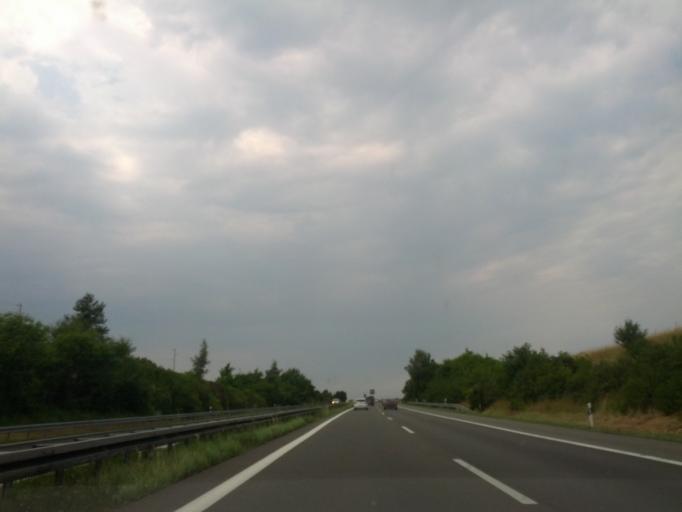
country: DE
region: Brandenburg
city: Fehrbellin
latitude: 52.8556
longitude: 12.7716
